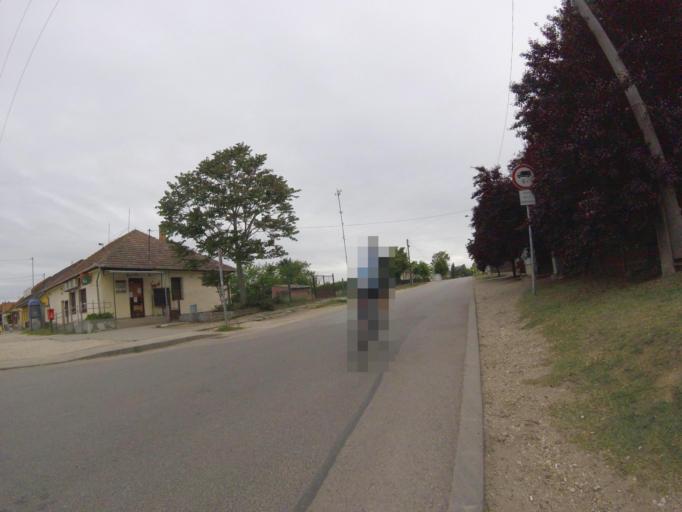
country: HU
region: Pest
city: Inarcs
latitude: 47.2548
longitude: 19.3295
